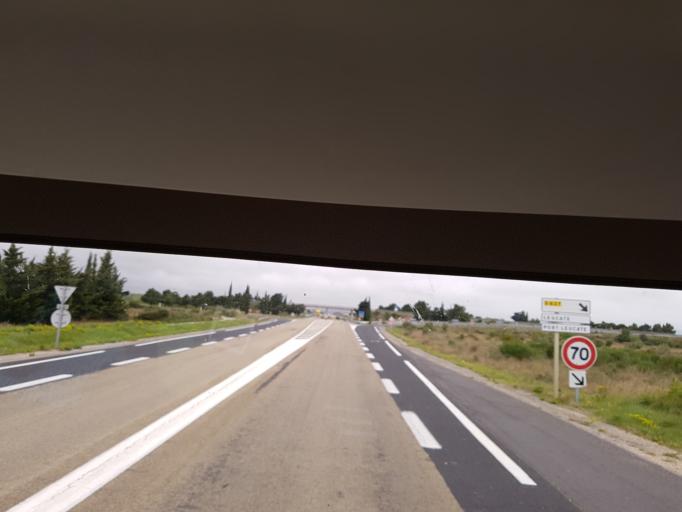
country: FR
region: Languedoc-Roussillon
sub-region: Departement de l'Aude
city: Leucate
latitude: 42.9339
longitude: 2.9920
